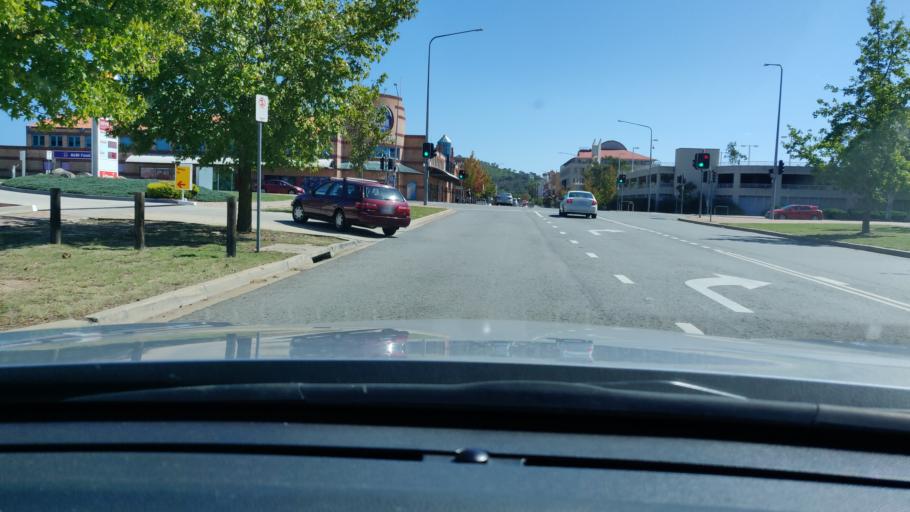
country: AU
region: Australian Capital Territory
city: Macarthur
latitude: -35.4185
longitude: 149.0697
